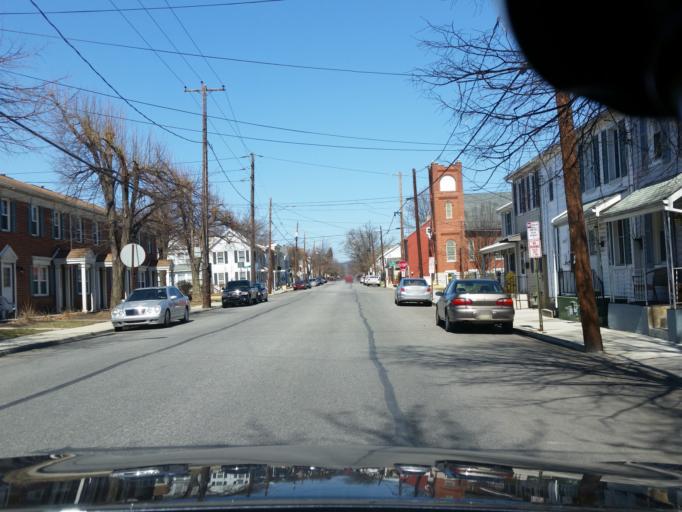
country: US
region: Pennsylvania
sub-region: Cumberland County
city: Carlisle
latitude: 40.2061
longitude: -77.1932
